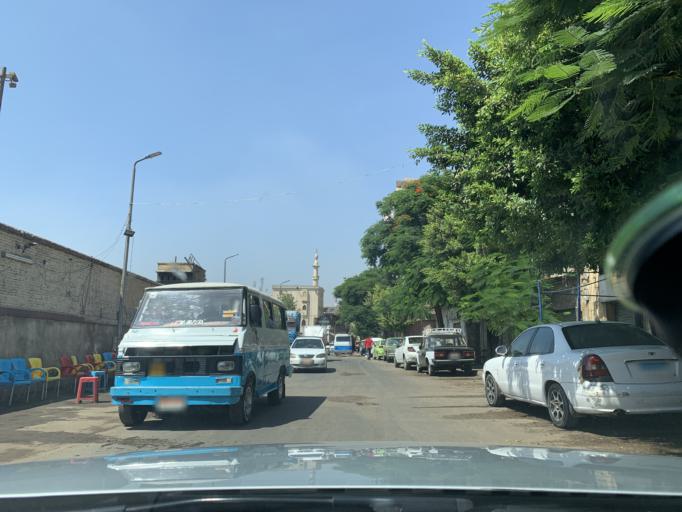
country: EG
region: Muhafazat al Qahirah
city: Cairo
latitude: 30.0693
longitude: 31.2548
